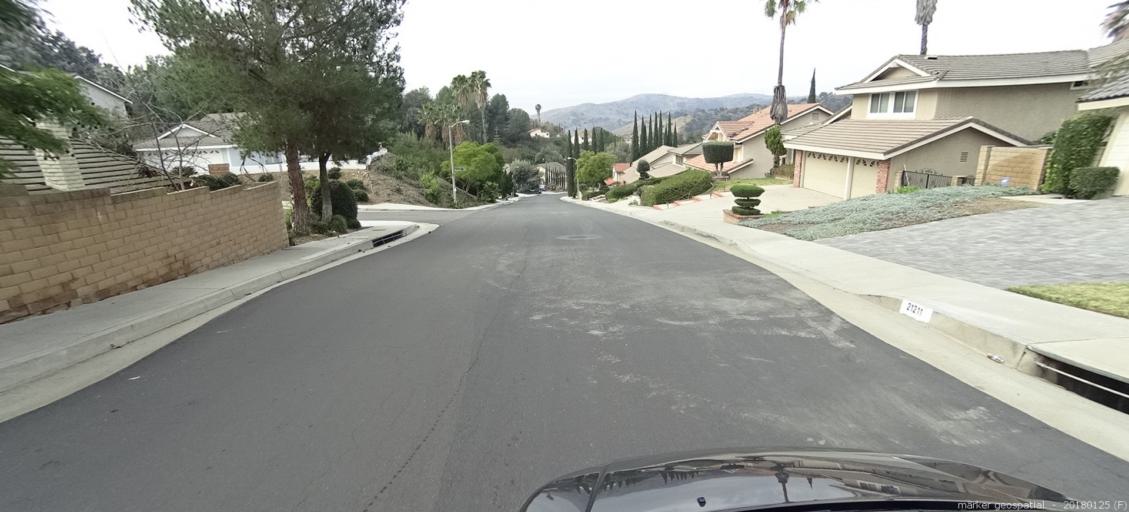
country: US
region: California
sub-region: Los Angeles County
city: Walnut
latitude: 33.9656
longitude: -117.8435
